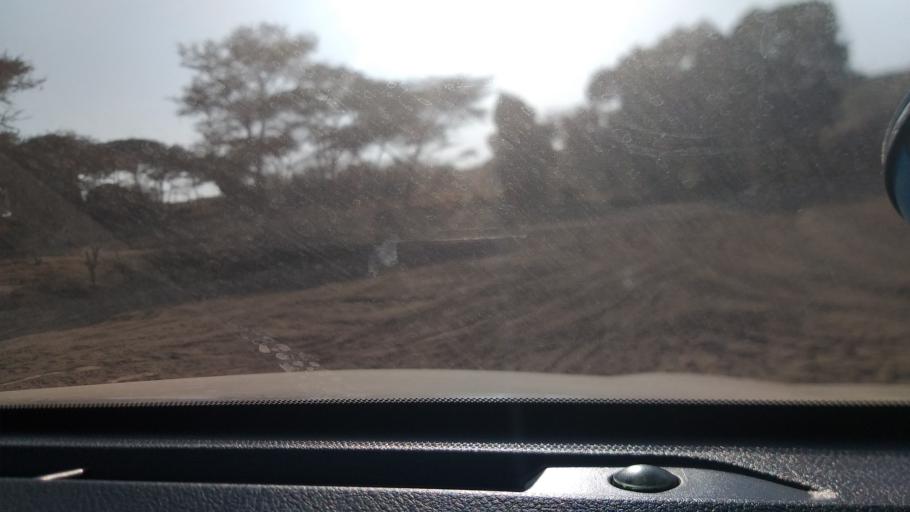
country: ET
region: Oromiya
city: Shashemene
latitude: 7.4864
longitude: 38.7248
